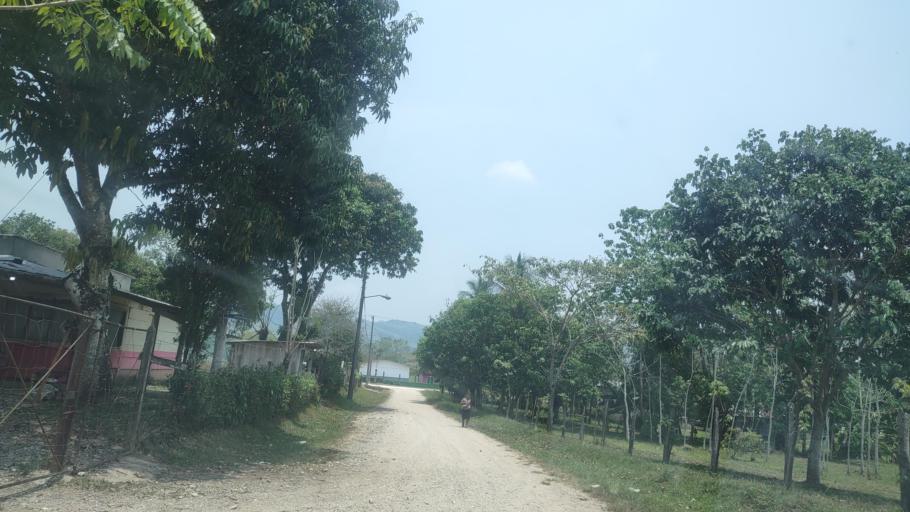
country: MX
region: Chiapas
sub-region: Tecpatan
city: Raudales Malpaso
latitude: 17.4584
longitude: -93.8021
